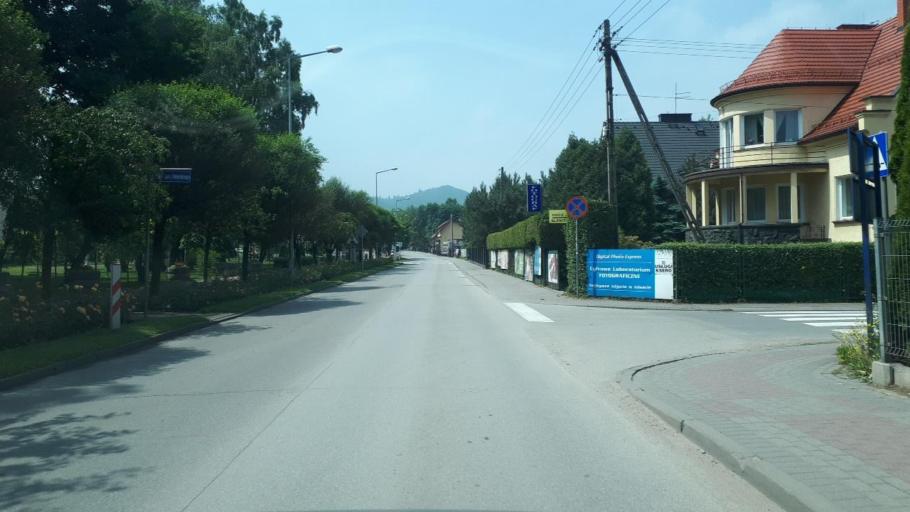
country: PL
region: Silesian Voivodeship
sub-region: Powiat cieszynski
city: Ustron
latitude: 49.7211
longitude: 18.8149
